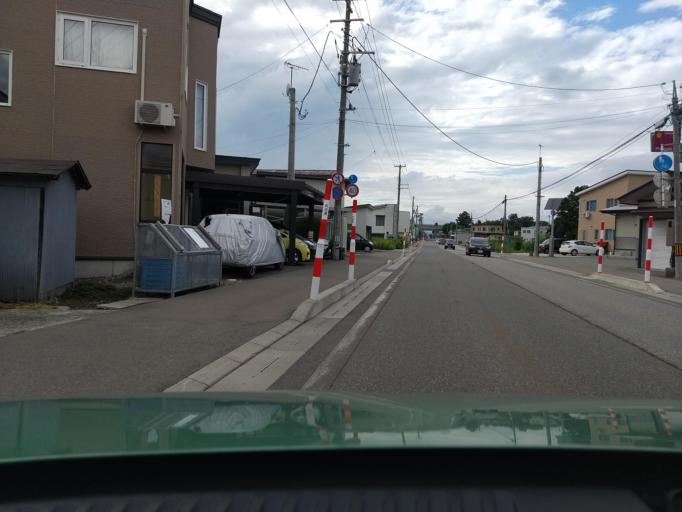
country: JP
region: Akita
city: Yuzawa
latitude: 39.2279
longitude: 140.5200
